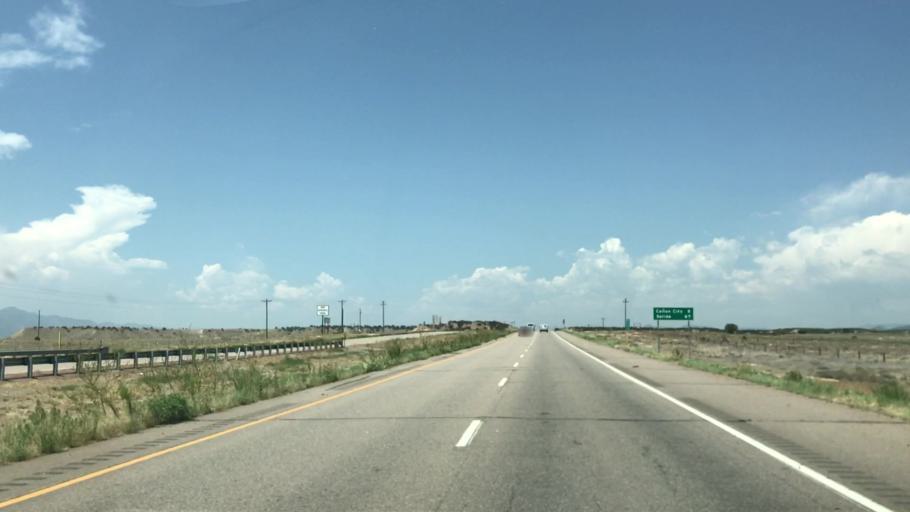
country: US
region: Colorado
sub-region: Fremont County
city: Penrose
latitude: 38.4216
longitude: -105.0570
